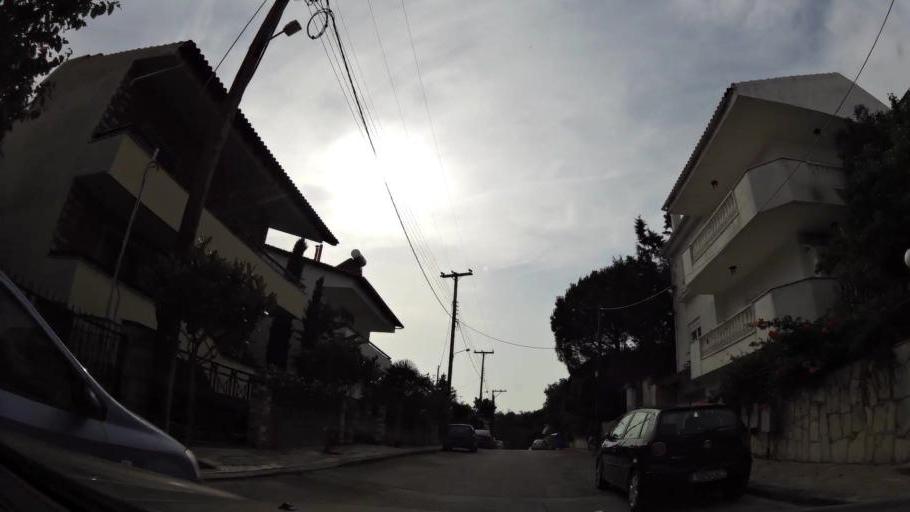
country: GR
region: Central Macedonia
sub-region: Nomos Thessalonikis
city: Oraiokastro
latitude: 40.7340
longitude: 22.9176
